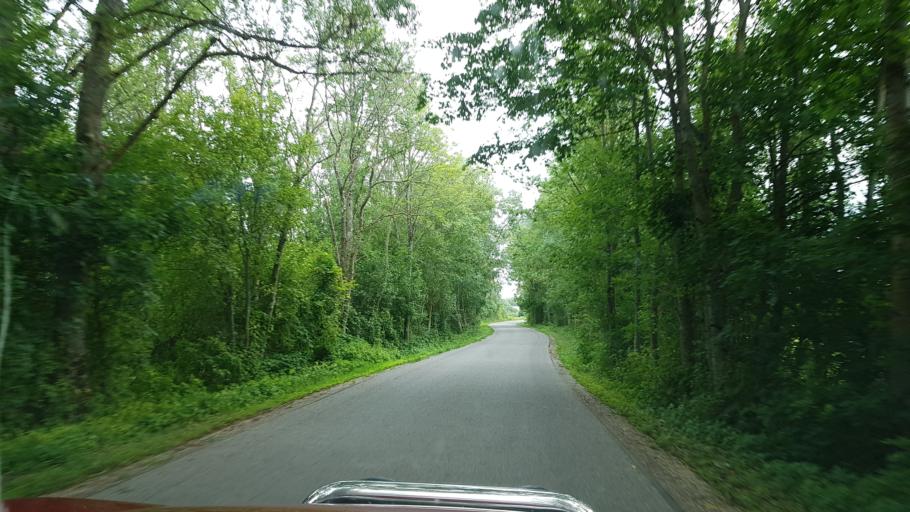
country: EE
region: Laeaene
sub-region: Ridala Parish
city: Uuemoisa
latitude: 58.9755
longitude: 23.7700
